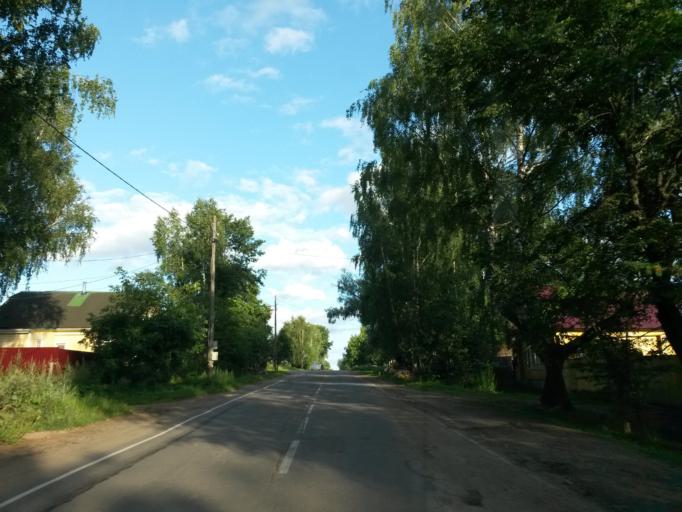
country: RU
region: Jaroslavl
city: Tutayev
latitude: 57.8862
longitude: 39.5423
